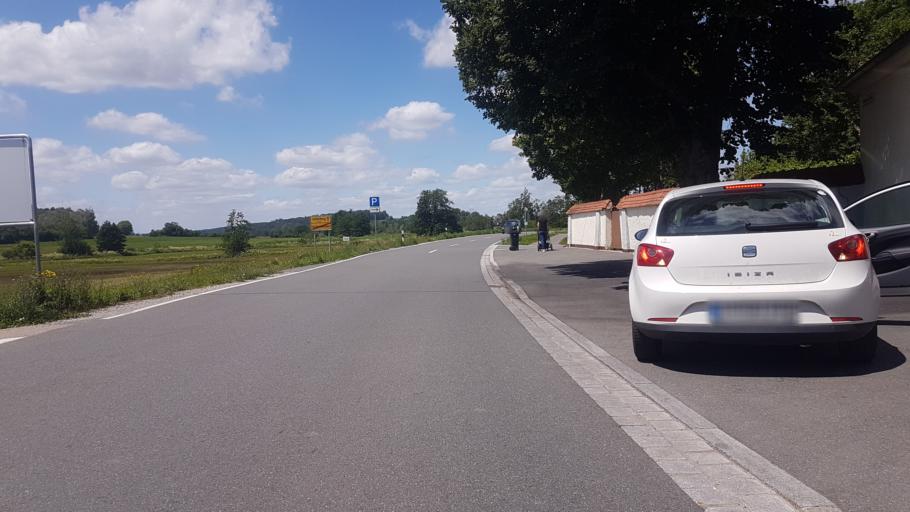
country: DE
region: Bavaria
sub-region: Regierungsbezirk Mittelfranken
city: Leutershausen
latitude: 49.3027
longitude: 10.4031
